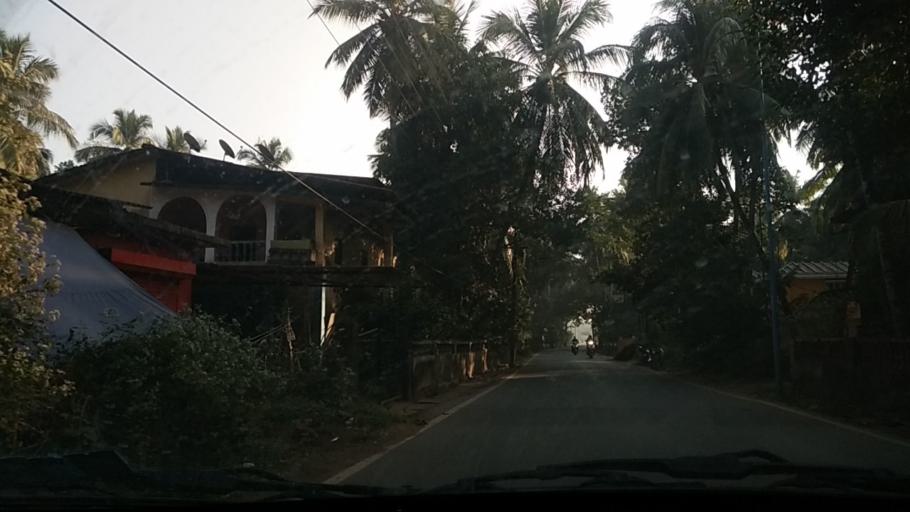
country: IN
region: Goa
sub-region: South Goa
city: Cuncolim
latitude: 15.1827
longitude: 74.0024
